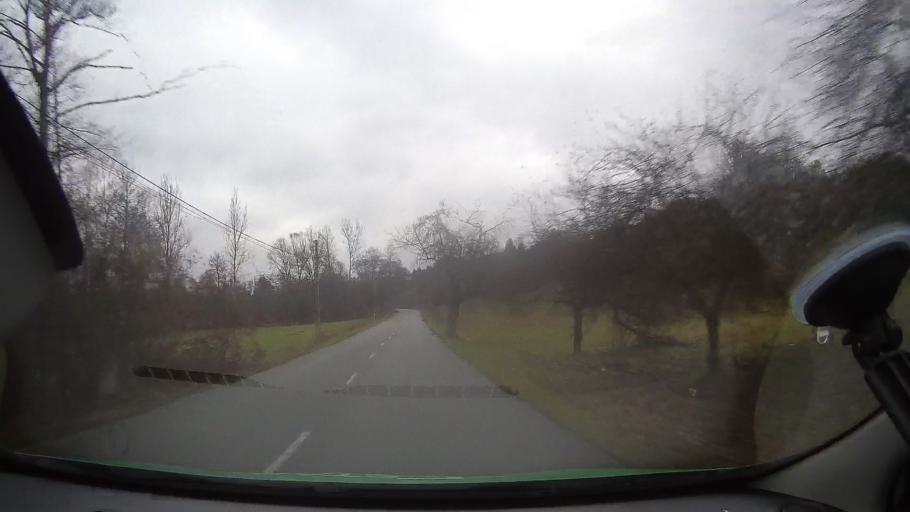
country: RO
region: Hunedoara
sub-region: Comuna Tomesti
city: Tomesti
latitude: 46.2015
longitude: 22.6607
